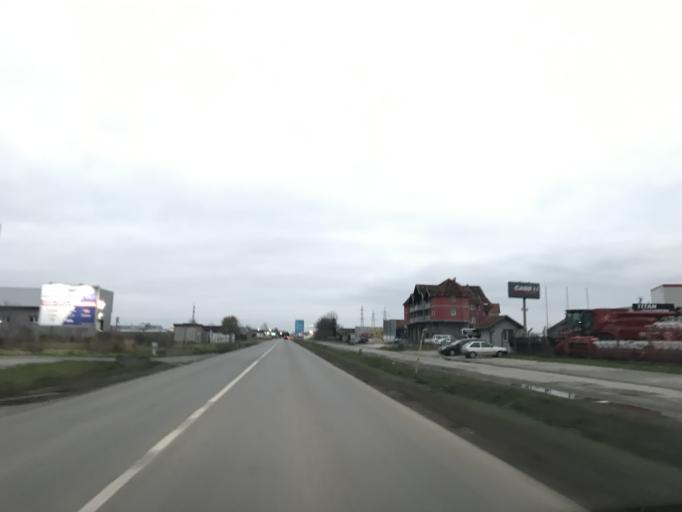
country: RS
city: Rumenka
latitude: 45.2833
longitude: 19.7701
